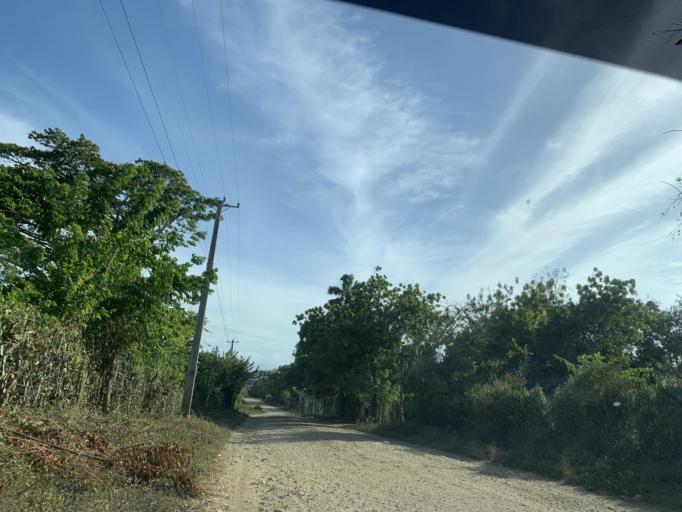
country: DO
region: Puerto Plata
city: Luperon
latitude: 19.8662
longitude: -70.9461
